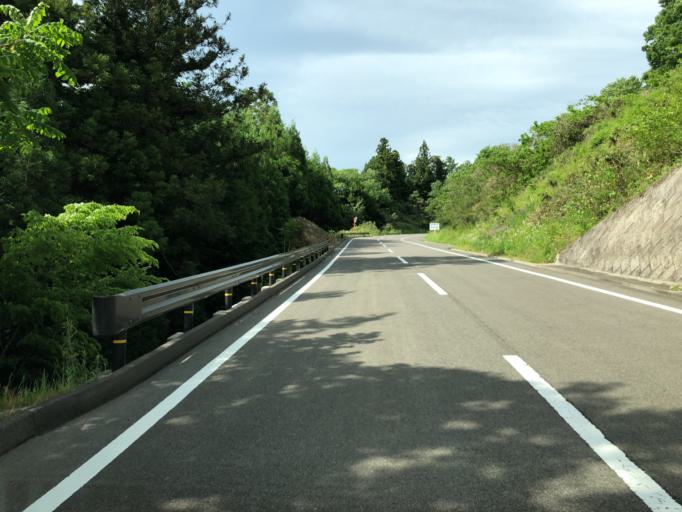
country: JP
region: Fukushima
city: Nihommatsu
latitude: 37.6018
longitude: 140.5200
